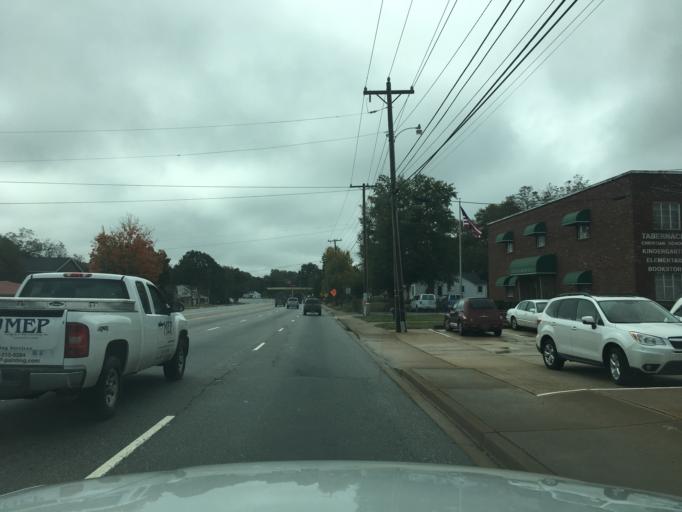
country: US
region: South Carolina
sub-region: Greenville County
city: Welcome
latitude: 34.8277
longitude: -82.4471
